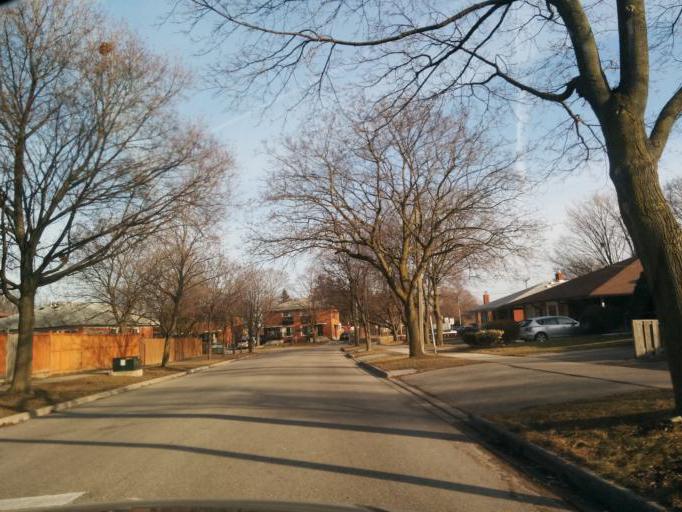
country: CA
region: Ontario
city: Etobicoke
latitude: 43.6091
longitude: -79.5979
